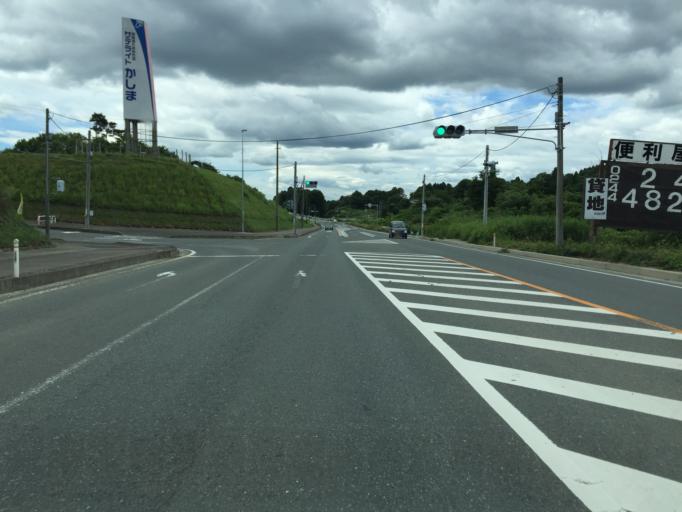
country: JP
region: Fukushima
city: Namie
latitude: 37.7298
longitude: 140.9533
